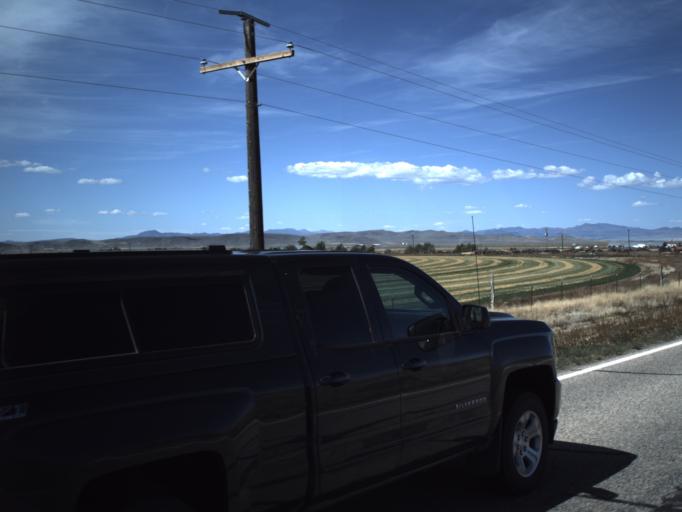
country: US
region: Utah
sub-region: Washington County
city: Enterprise
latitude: 37.6086
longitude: -113.6612
